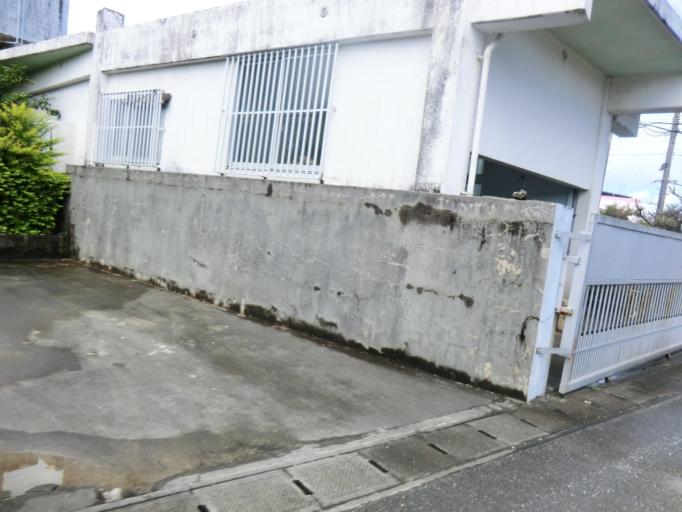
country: JP
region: Okinawa
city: Itoman
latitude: 26.0911
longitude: 127.6807
